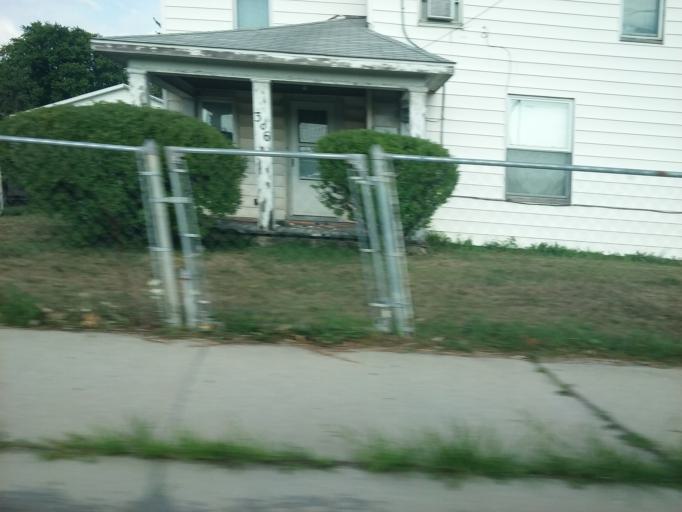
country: US
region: Ohio
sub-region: Wood County
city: Bowling Green
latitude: 41.3299
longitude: -83.6503
